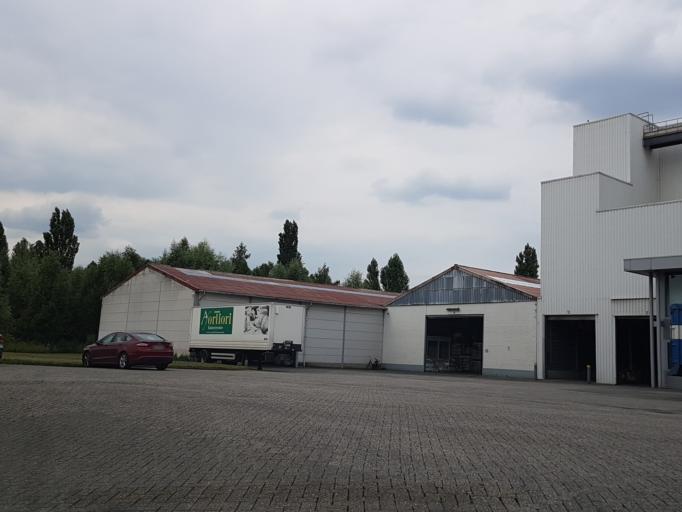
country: BE
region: Flanders
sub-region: Provincie Antwerpen
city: Schoten
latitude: 51.2407
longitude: 4.4895
